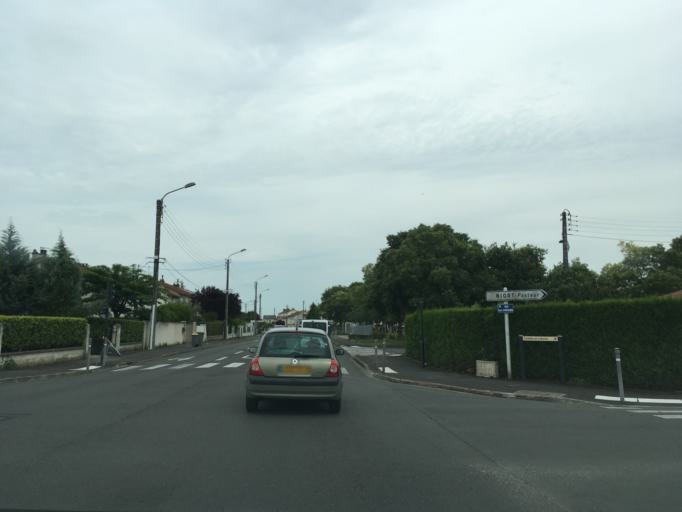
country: FR
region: Poitou-Charentes
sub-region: Departement des Deux-Sevres
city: Niort
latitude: 46.3139
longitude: -0.4699
